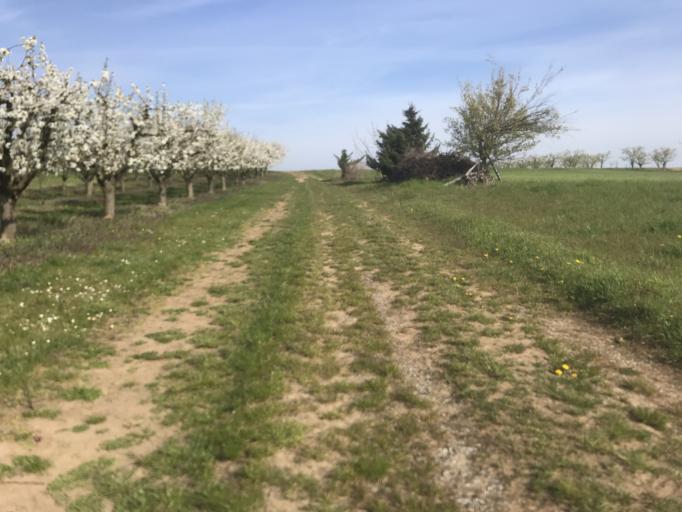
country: DE
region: Rheinland-Pfalz
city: Wackernheim
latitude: 49.9532
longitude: 8.1091
